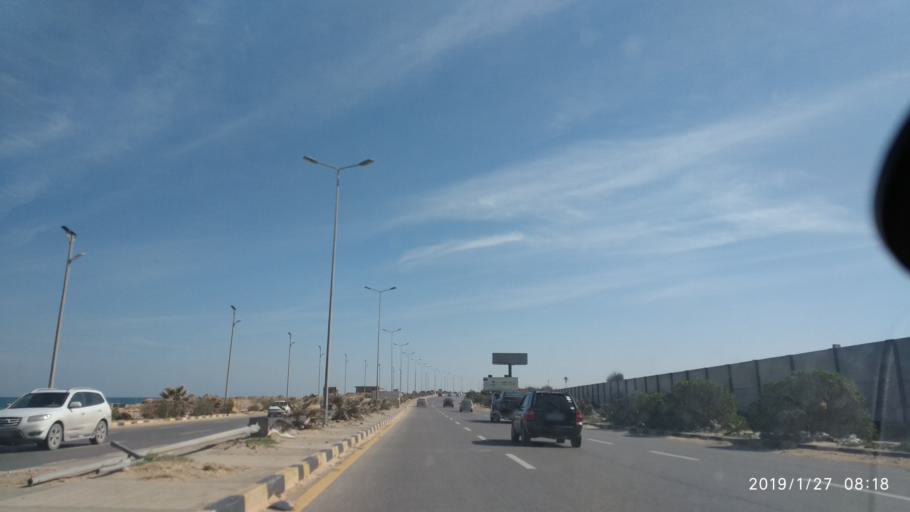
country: LY
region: Tripoli
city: Tagiura
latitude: 32.9023
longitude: 13.3042
